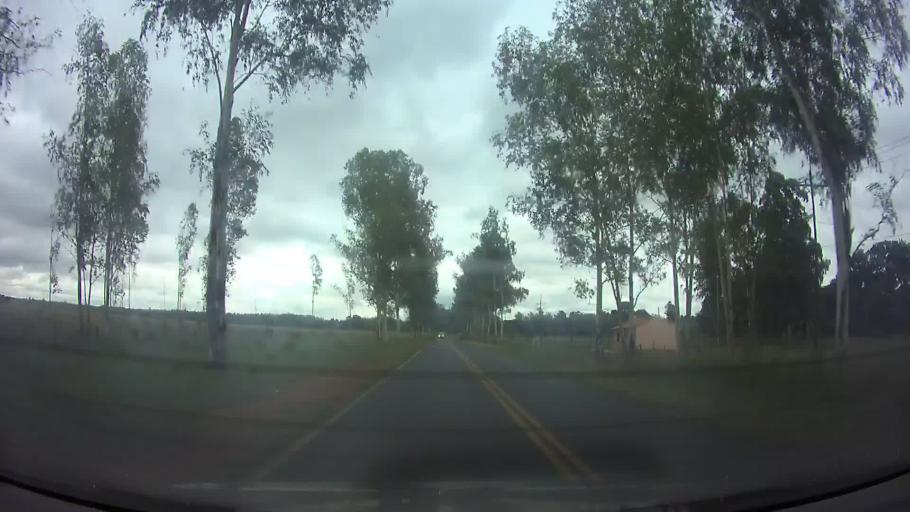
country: PY
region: Central
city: Nueva Italia
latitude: -25.5568
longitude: -57.5015
